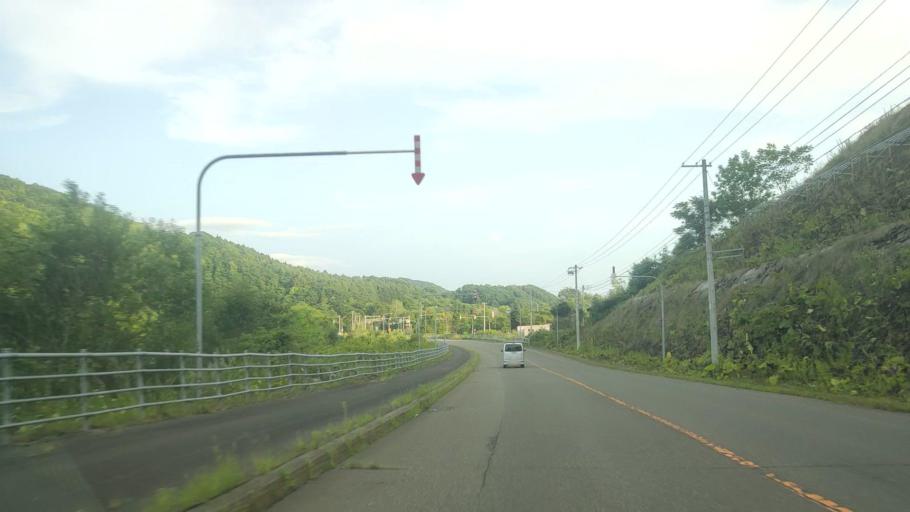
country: JP
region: Hokkaido
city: Iwamizawa
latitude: 43.0086
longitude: 142.0033
